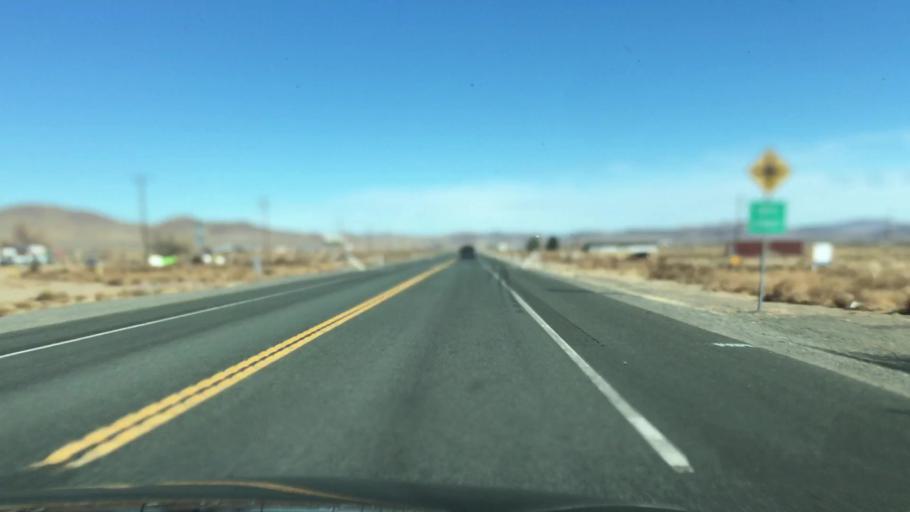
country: US
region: Nevada
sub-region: Lyon County
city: Silver Springs
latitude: 39.3962
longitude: -119.2793
